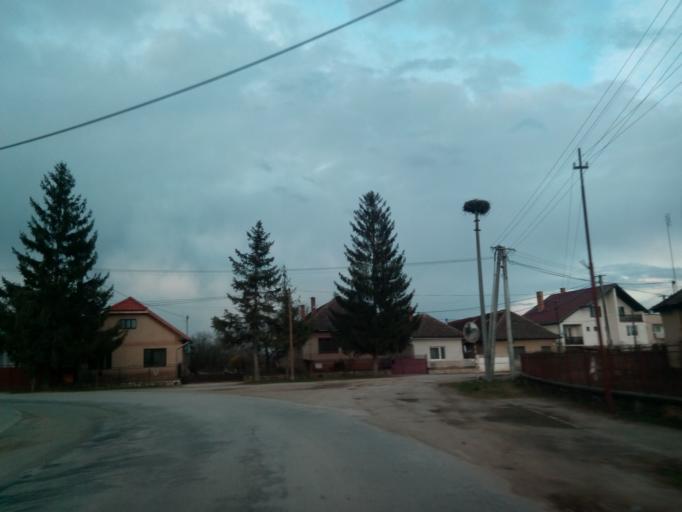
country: SK
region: Kosicky
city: Moldava nad Bodvou
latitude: 48.5876
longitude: 20.9944
